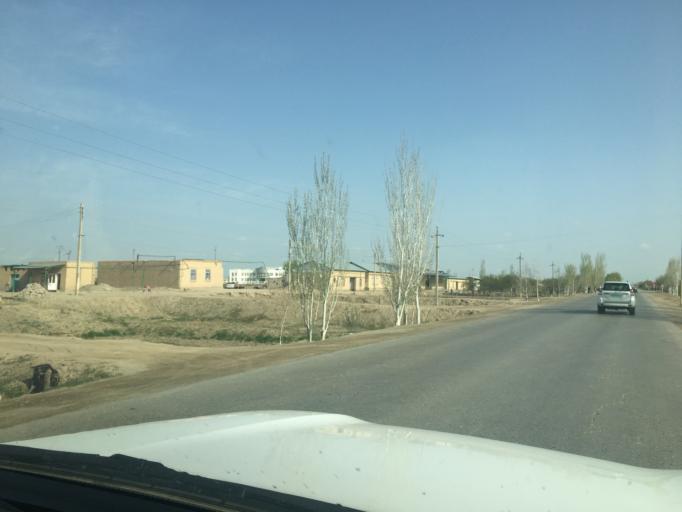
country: TM
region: Lebap
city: Farap
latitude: 39.2009
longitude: 63.5645
